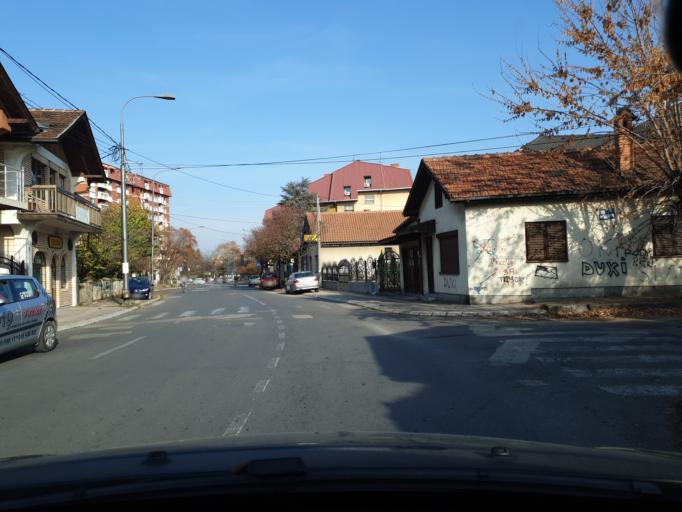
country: RS
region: Central Serbia
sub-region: Zajecarski Okrug
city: Zajecar
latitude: 43.9010
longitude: 22.2691
